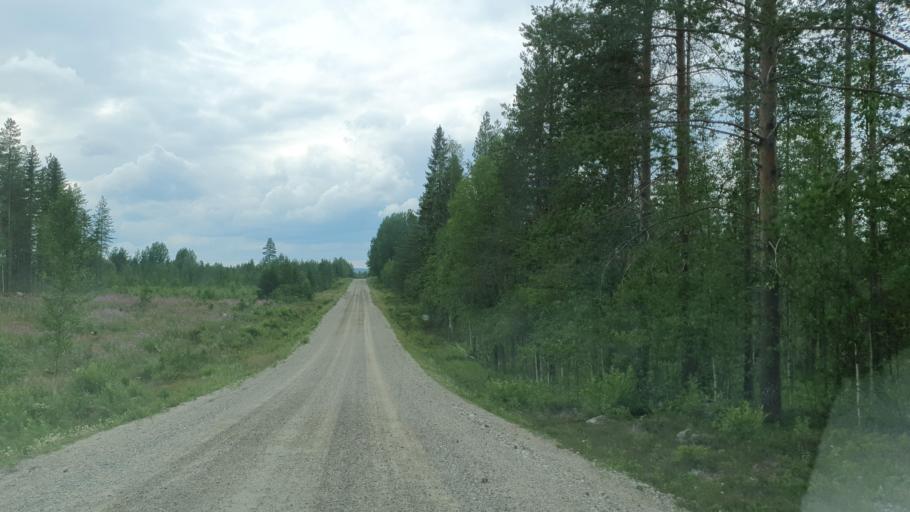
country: FI
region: Kainuu
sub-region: Kehys-Kainuu
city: Kuhmo
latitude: 64.4873
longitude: 29.7200
